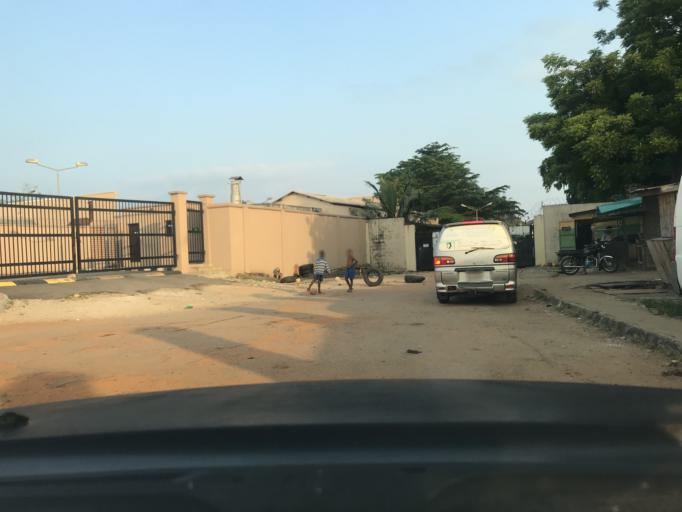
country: NG
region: Lagos
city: Festac Town
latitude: 6.4648
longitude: 3.3051
